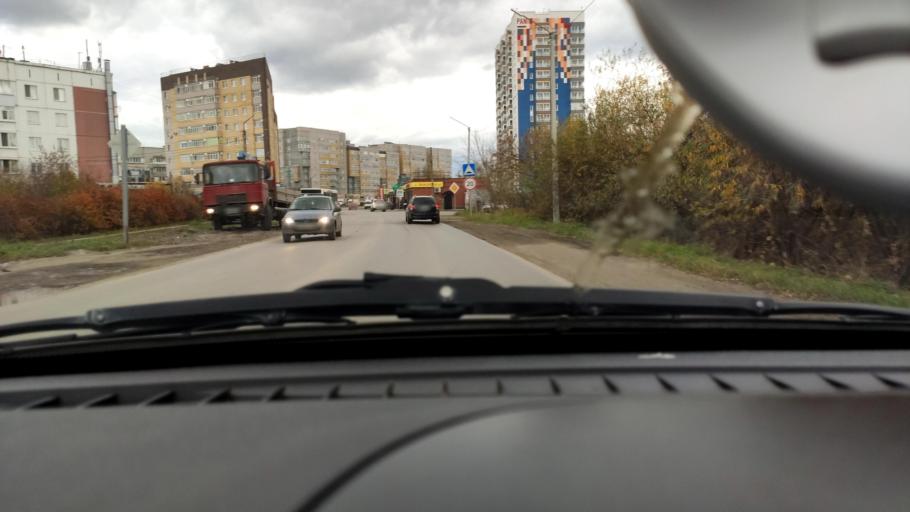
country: RU
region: Perm
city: Kondratovo
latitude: 57.9753
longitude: 56.1103
